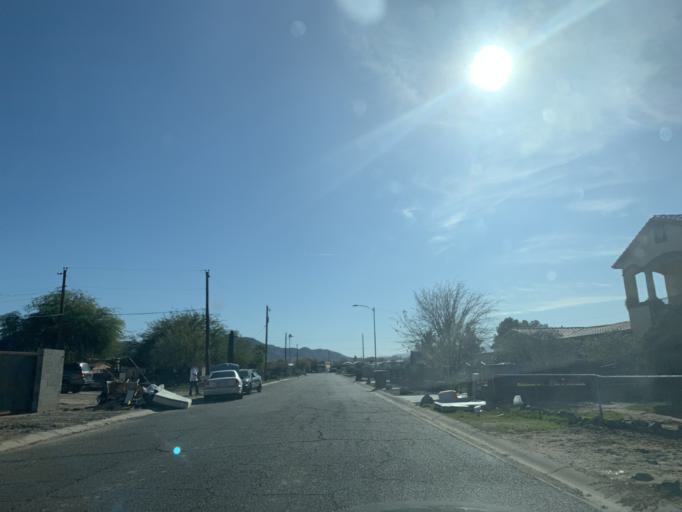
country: US
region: Arizona
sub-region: Maricopa County
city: Laveen
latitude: 33.3948
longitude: -112.1409
